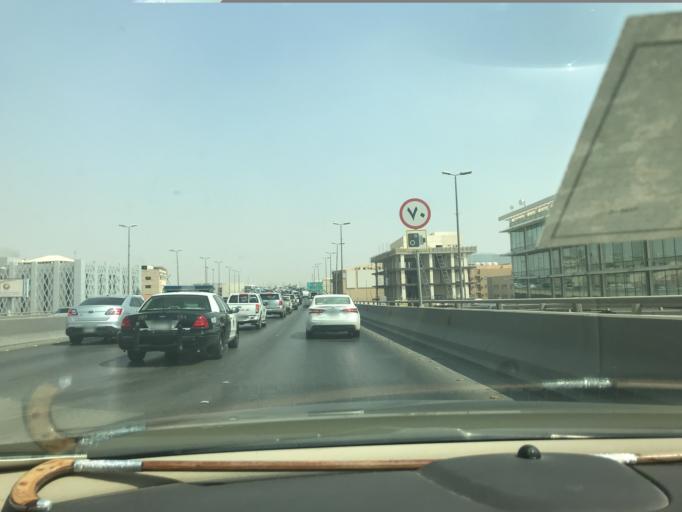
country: SA
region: Ar Riyad
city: Riyadh
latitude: 24.6926
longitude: 46.7194
